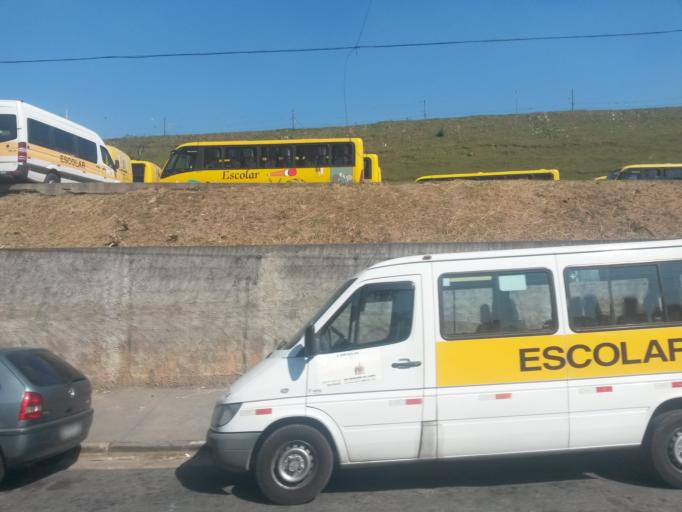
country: BR
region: Sao Paulo
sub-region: Sao Bernardo Do Campo
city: Sao Bernardo do Campo
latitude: -23.7388
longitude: -46.5276
